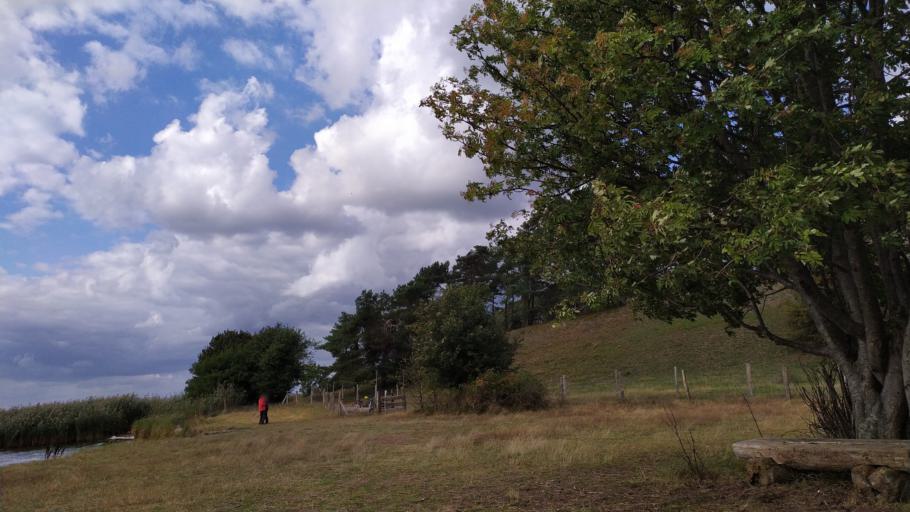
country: DE
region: Mecklenburg-Vorpommern
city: Lassan
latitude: 54.0012
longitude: 13.8579
